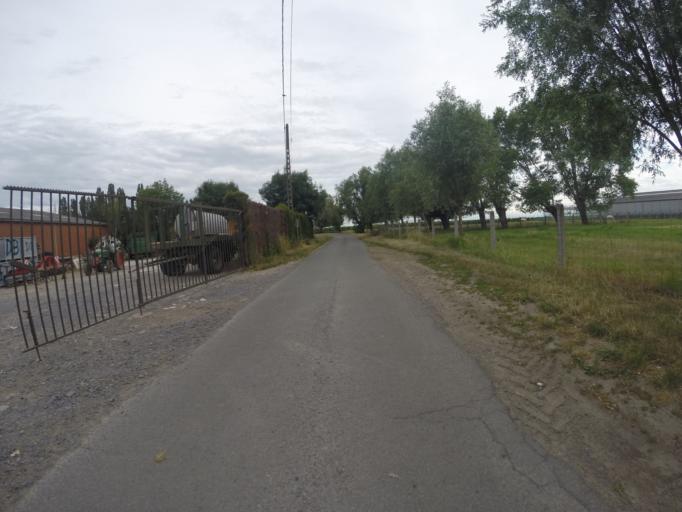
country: BE
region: Flanders
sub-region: Provincie West-Vlaanderen
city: Ruiselede
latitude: 51.0090
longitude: 3.3913
